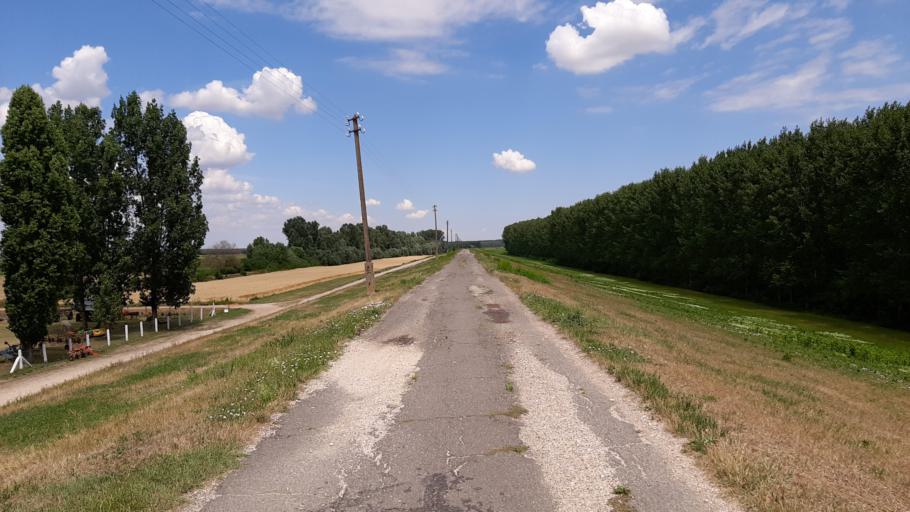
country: HU
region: Csongrad
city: Csongrad
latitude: 46.6522
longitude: 20.1843
